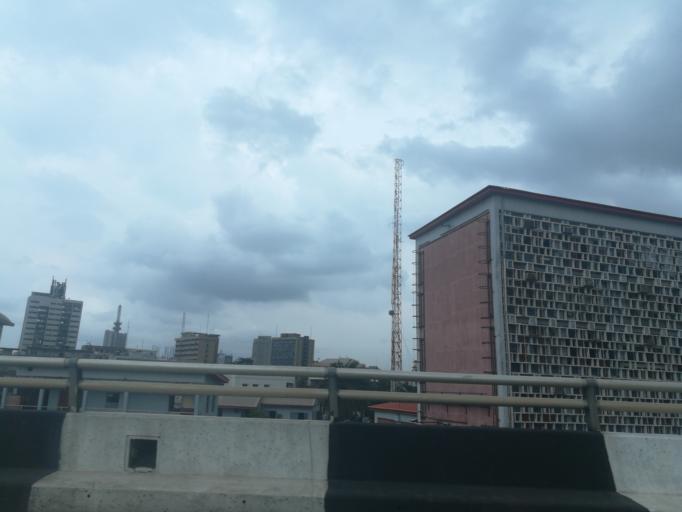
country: NG
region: Lagos
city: Lagos
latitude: 6.4483
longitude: 3.4076
